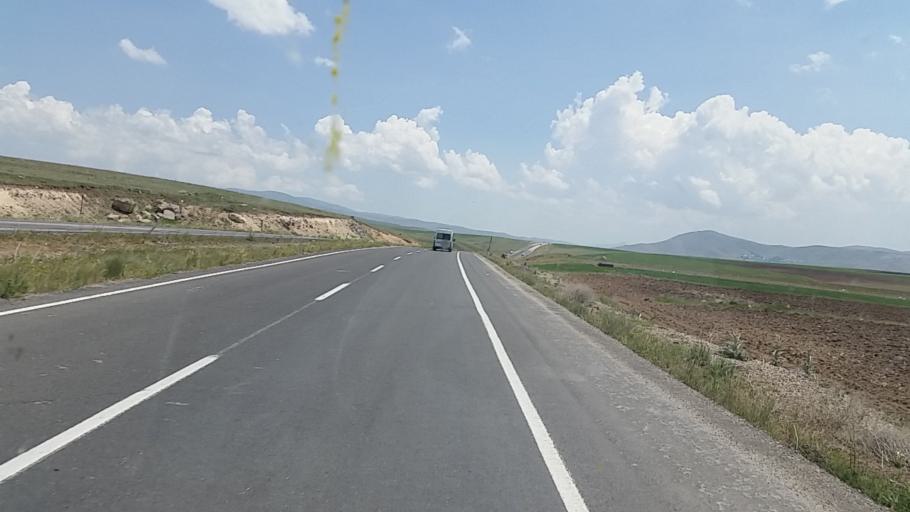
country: TR
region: Agri
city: Taslicay
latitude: 39.6327
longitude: 43.4111
